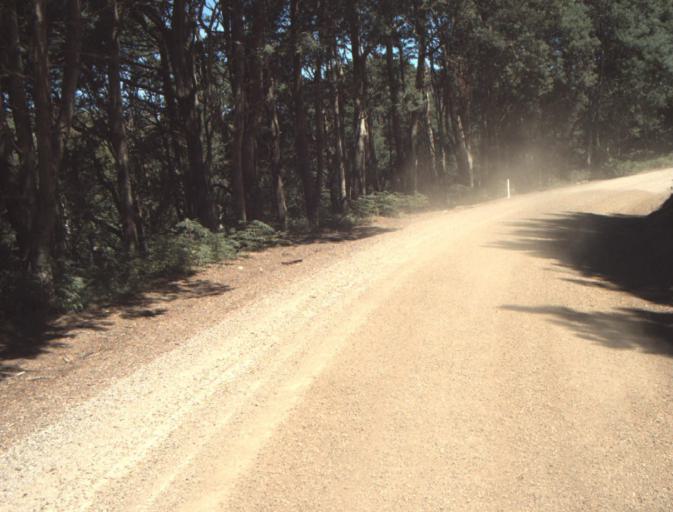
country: AU
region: Tasmania
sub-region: Dorset
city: Scottsdale
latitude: -41.3213
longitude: 147.4543
